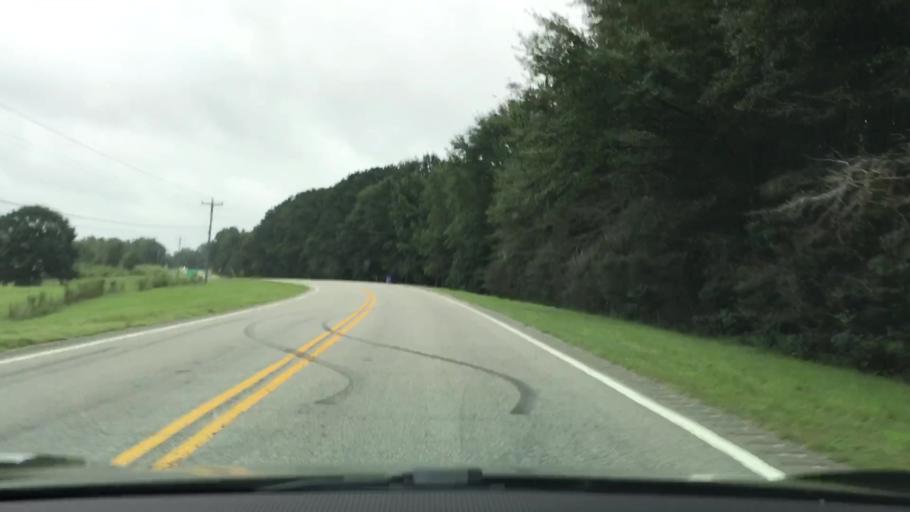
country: US
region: Alabama
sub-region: Pike County
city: Troy
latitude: 31.6142
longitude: -85.9868
